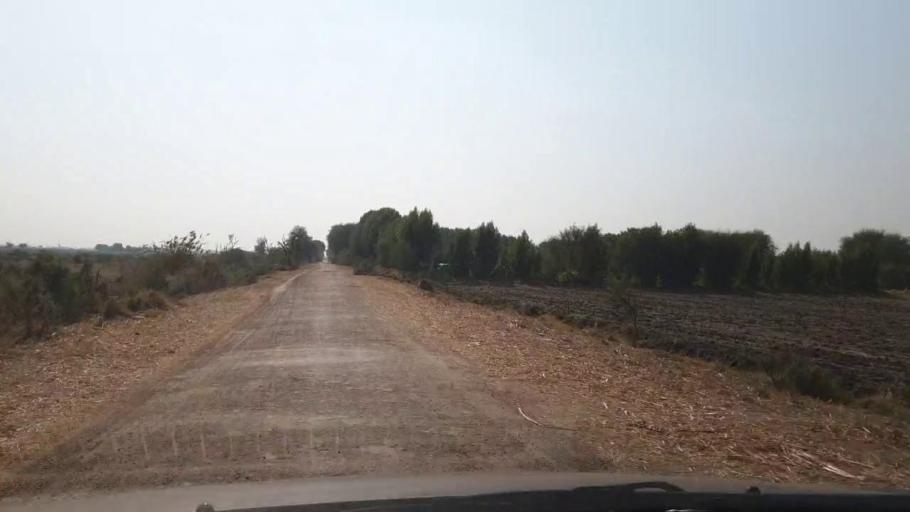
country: PK
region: Sindh
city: Jhol
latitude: 25.8406
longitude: 68.9875
